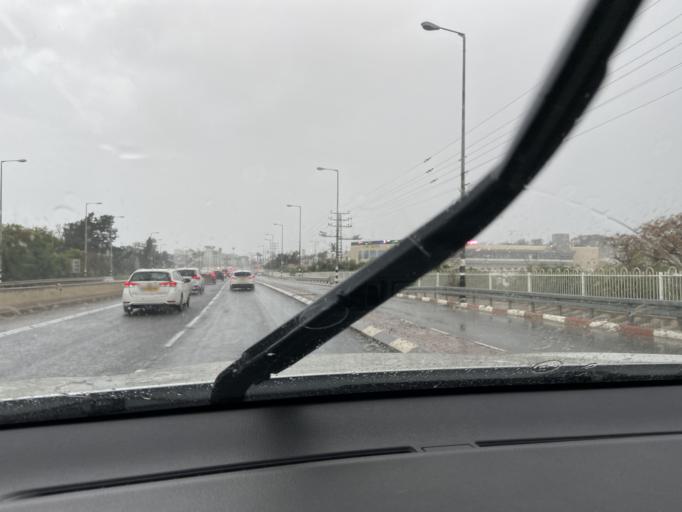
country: IL
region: Northern District
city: El Mazra`a
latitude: 32.9847
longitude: 35.0952
